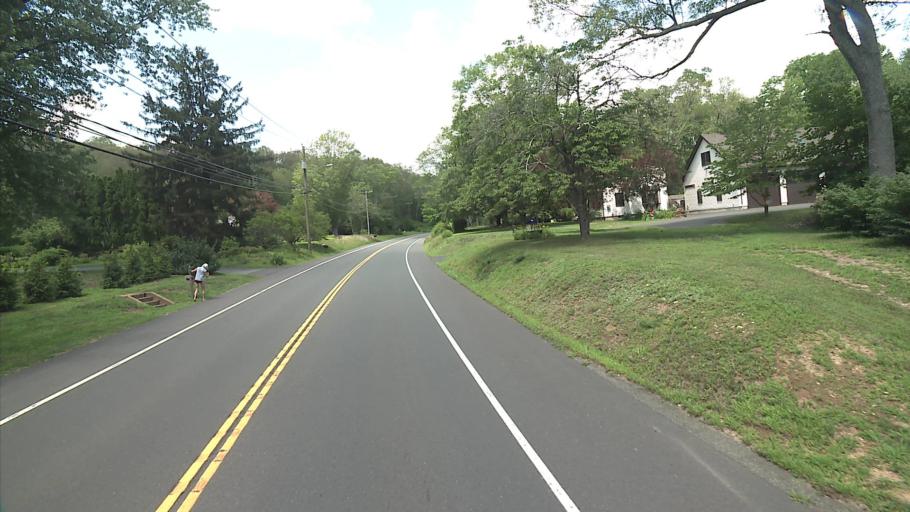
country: US
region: Connecticut
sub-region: Middlesex County
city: East Haddam
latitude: 41.4521
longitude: -72.4789
